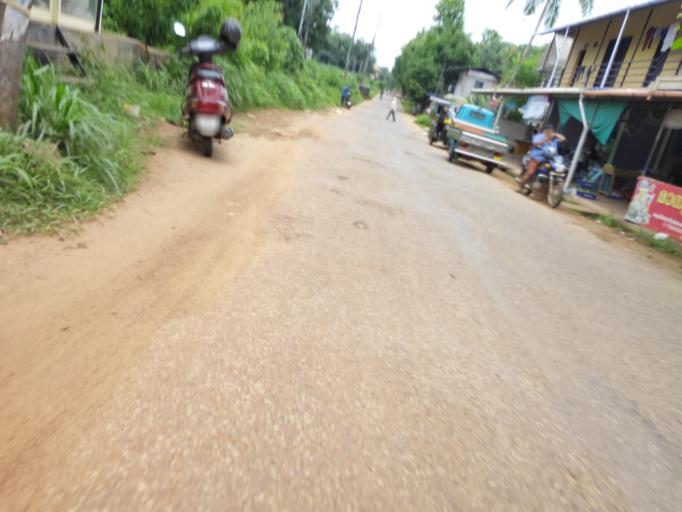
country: IN
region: Kerala
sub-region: Malappuram
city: Manjeri
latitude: 11.2358
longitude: 76.2854
